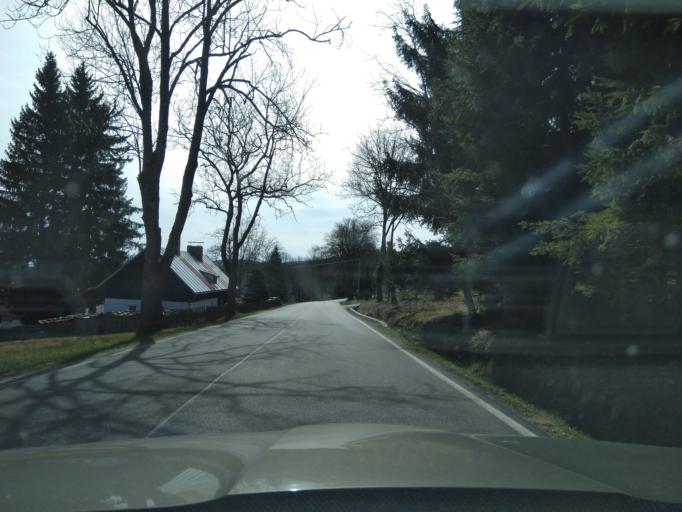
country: CZ
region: Jihocesky
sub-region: Okres Prachatice
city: Stachy
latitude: 49.0890
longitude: 13.6389
